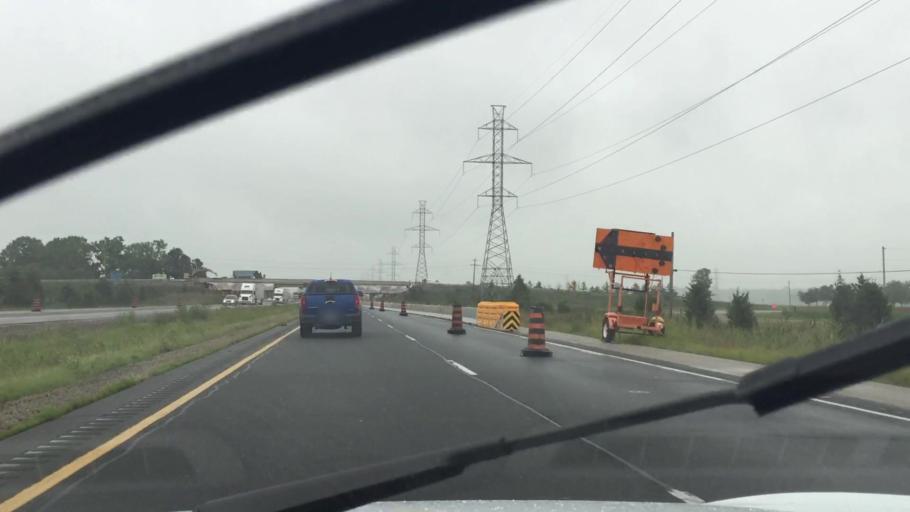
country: CA
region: Ontario
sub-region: Lambton County
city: Walpole Island
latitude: 42.3673
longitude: -82.1436
